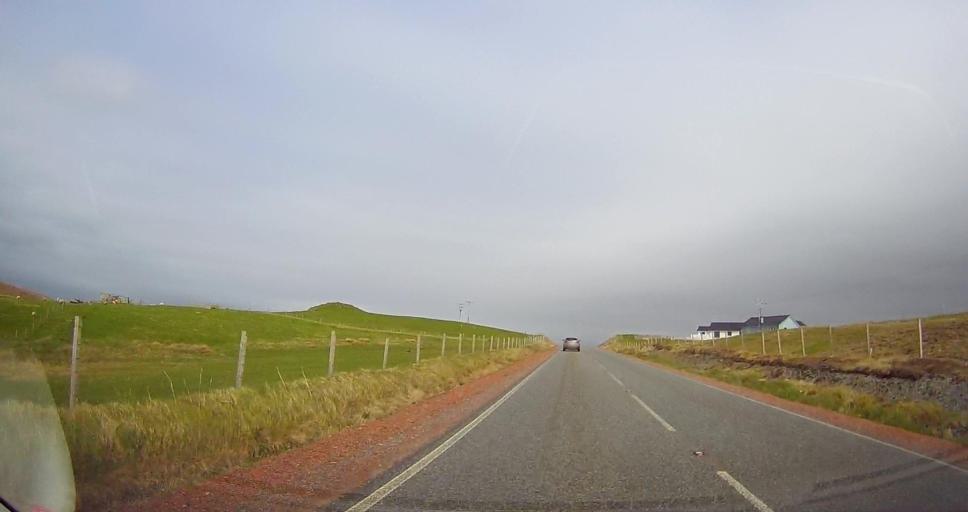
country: GB
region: Scotland
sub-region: Shetland Islands
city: Sandwick
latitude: 60.1190
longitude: -1.2906
